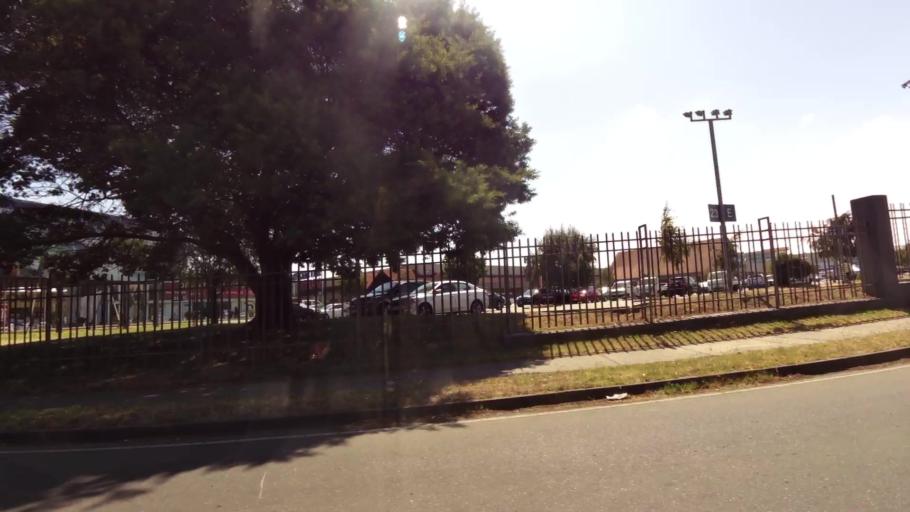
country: CL
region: Biobio
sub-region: Provincia de Concepcion
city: Concepcion
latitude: -36.7979
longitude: -73.0684
